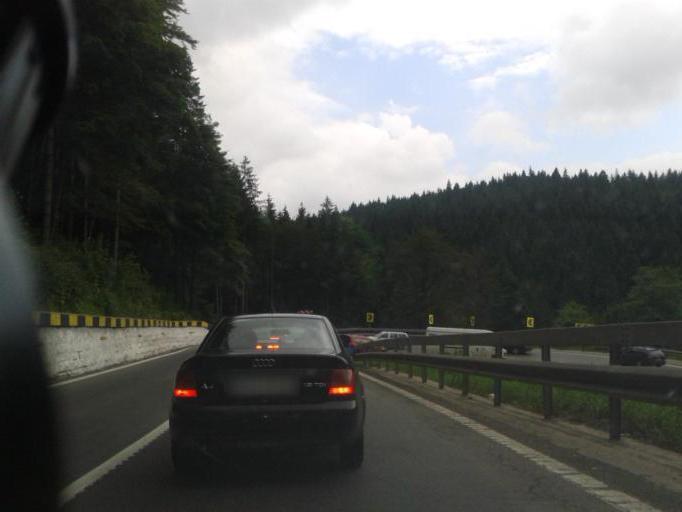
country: RO
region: Brasov
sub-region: Oras Predeal
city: Predeal
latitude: 45.5187
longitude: 25.5754
